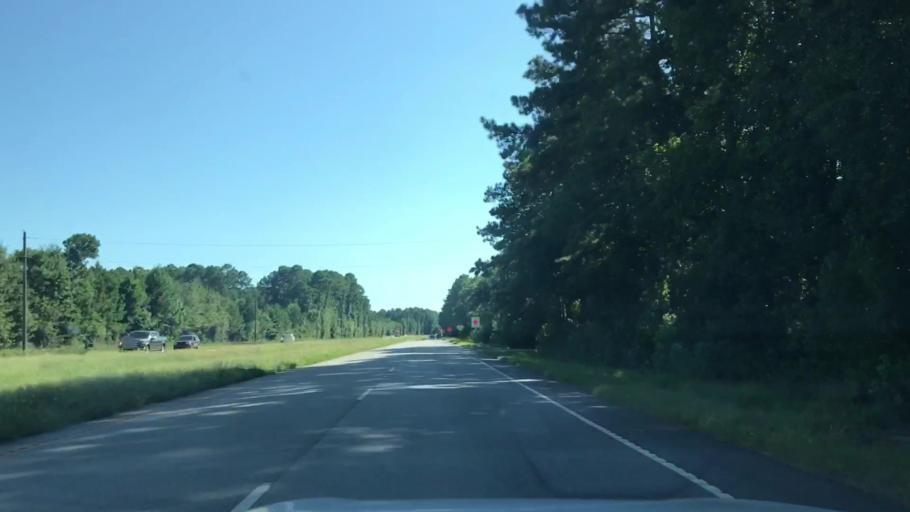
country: US
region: South Carolina
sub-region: Charleston County
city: Awendaw
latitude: 33.1072
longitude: -79.4631
